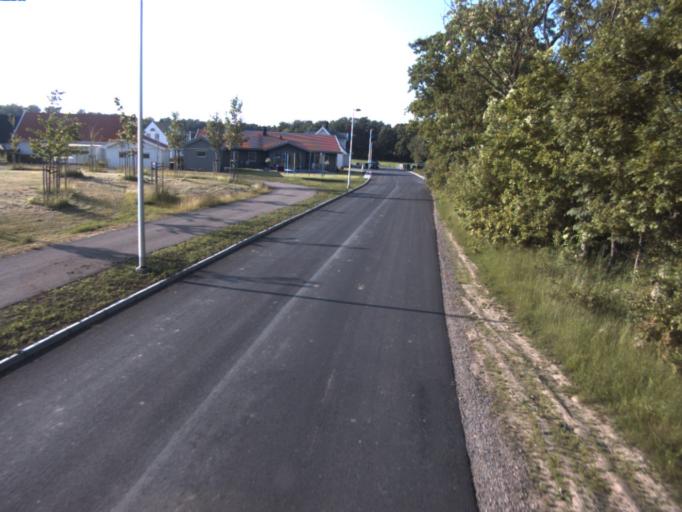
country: SE
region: Skane
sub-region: Helsingborg
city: Helsingborg
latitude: 56.0987
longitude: 12.6637
